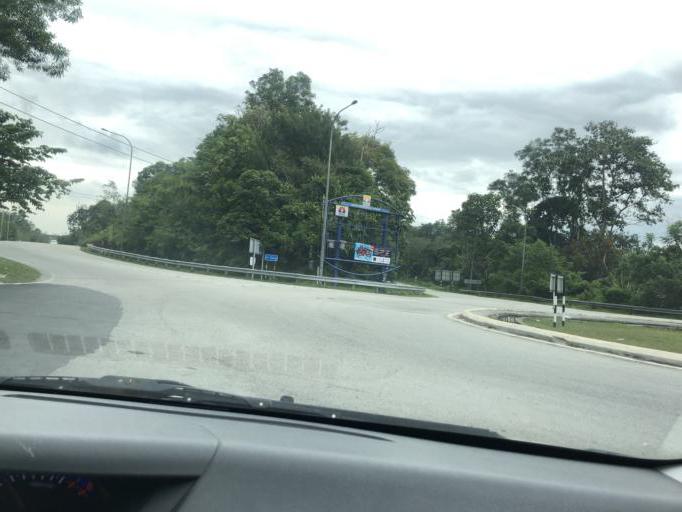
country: MY
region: Putrajaya
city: Putrajaya
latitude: 2.9221
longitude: 101.7473
